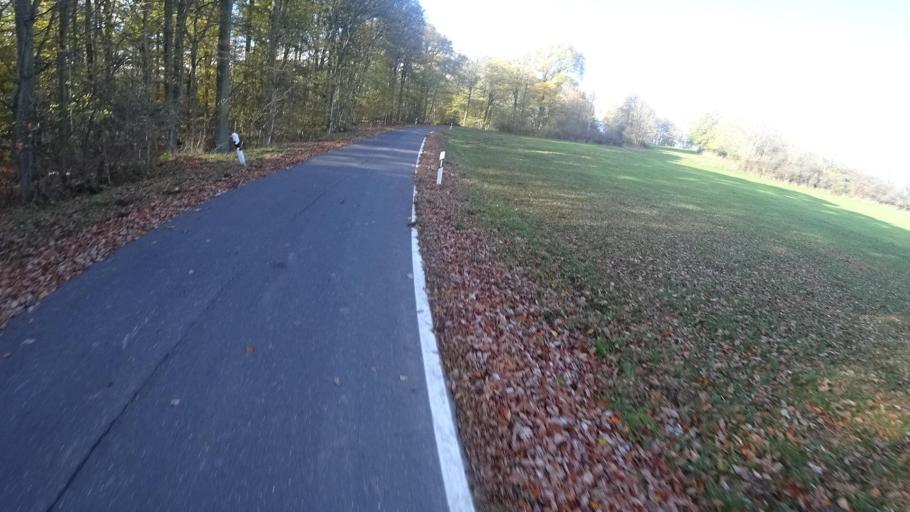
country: DE
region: Rheinland-Pfalz
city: Berg
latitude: 50.5231
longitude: 6.9511
